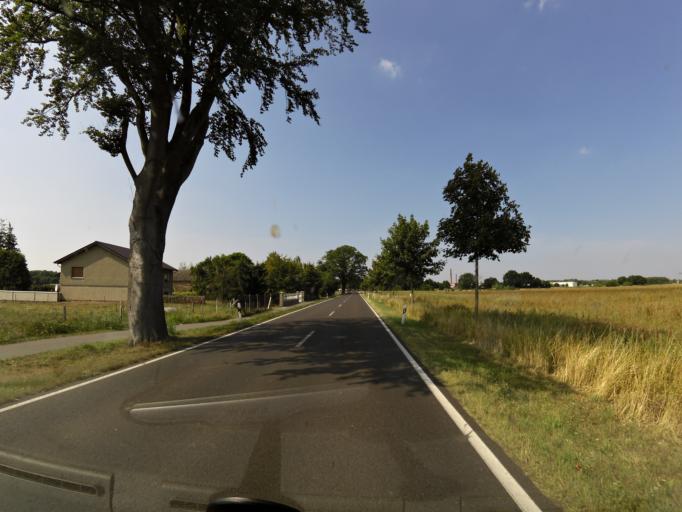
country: DE
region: Brandenburg
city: Zehdenick
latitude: 52.9728
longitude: 13.3559
